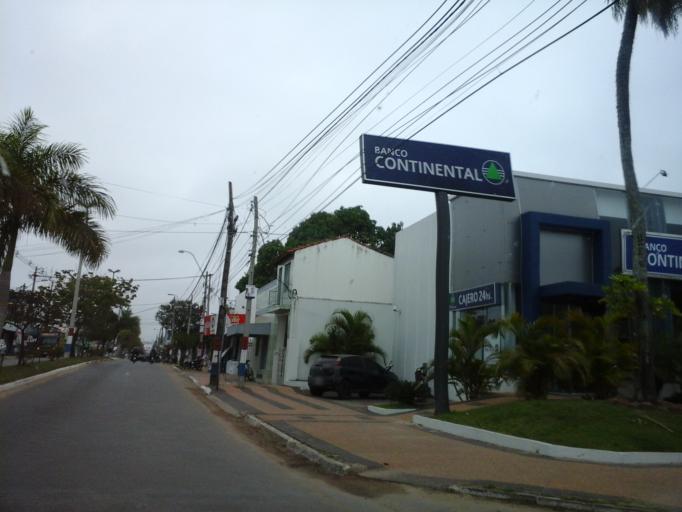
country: PY
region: Neembucu
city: Pilar
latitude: -26.8558
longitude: -58.2974
